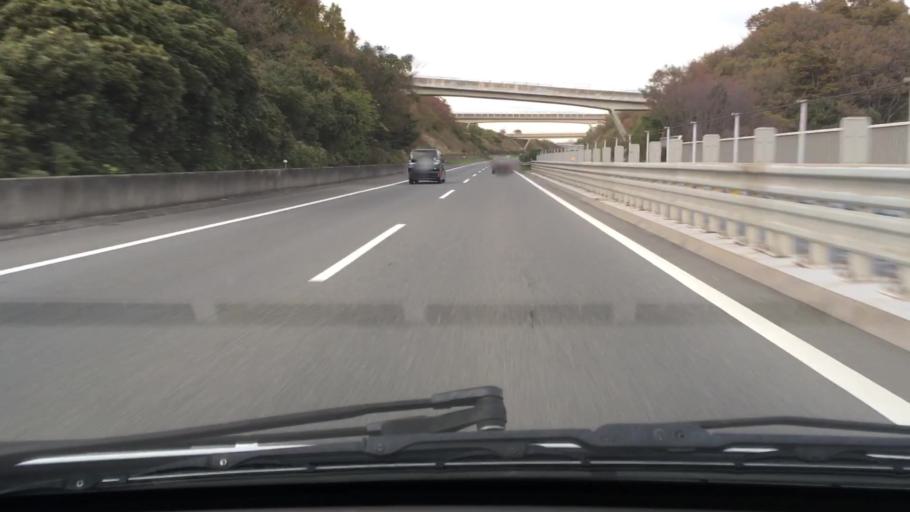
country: JP
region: Chiba
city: Kisarazu
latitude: 35.4164
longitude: 140.0114
